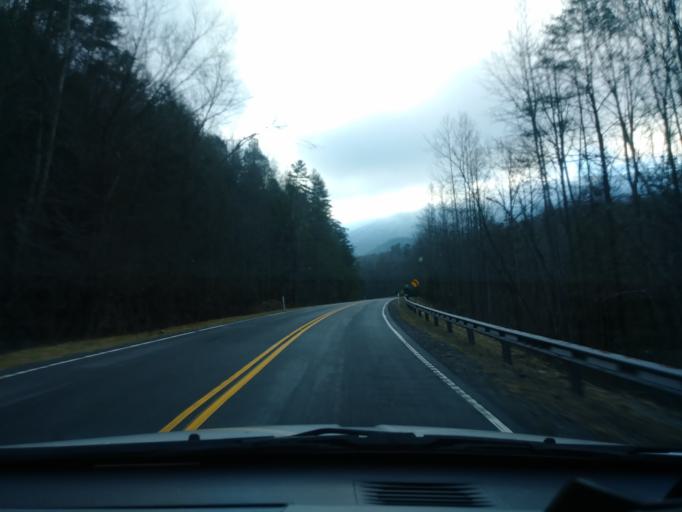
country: US
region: Tennessee
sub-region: Unicoi County
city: Unicoi
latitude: 36.1762
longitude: -82.3147
